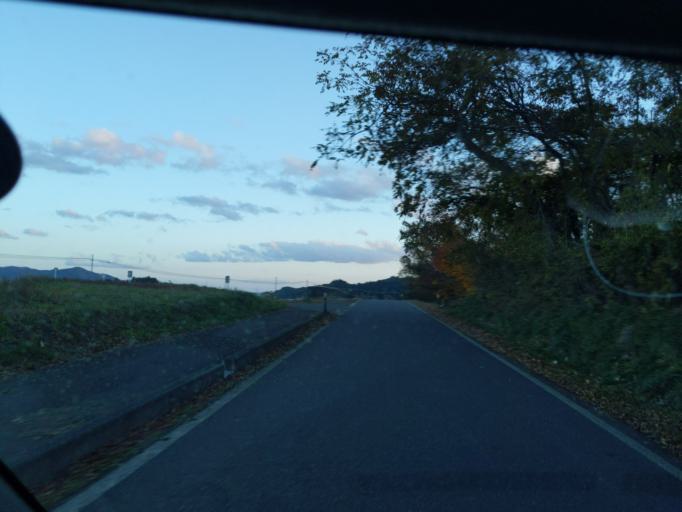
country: JP
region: Iwate
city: Ichinoseki
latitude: 39.0151
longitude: 141.0939
